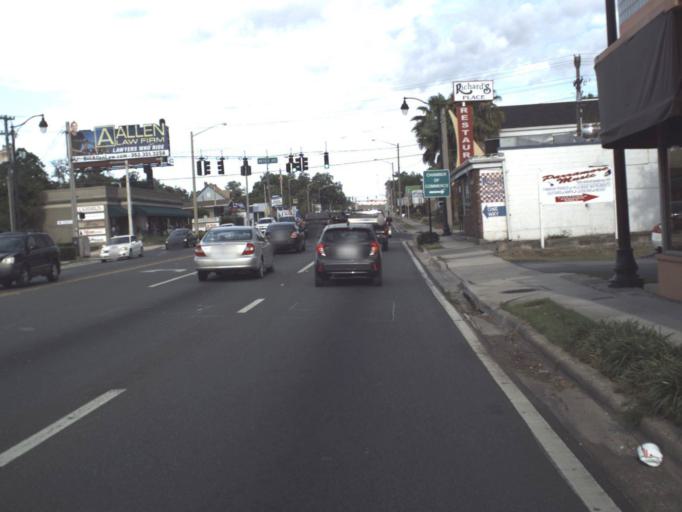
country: US
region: Florida
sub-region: Marion County
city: Ocala
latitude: 29.1870
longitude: -82.1342
